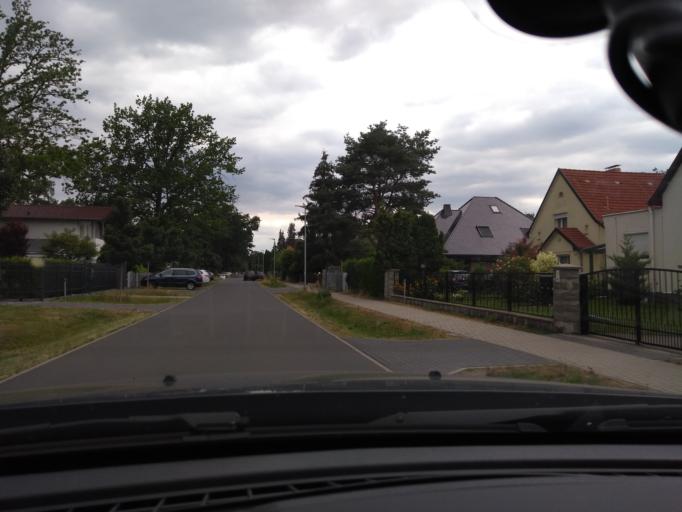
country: DE
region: Brandenburg
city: Dallgow-Doeberitz
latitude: 52.5563
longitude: 13.0690
